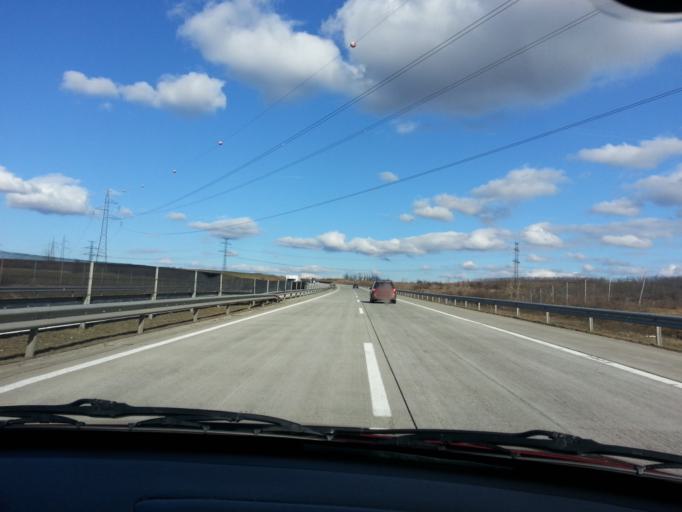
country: HU
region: Pest
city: Nagytarcsa
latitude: 47.5431
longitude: 19.3102
